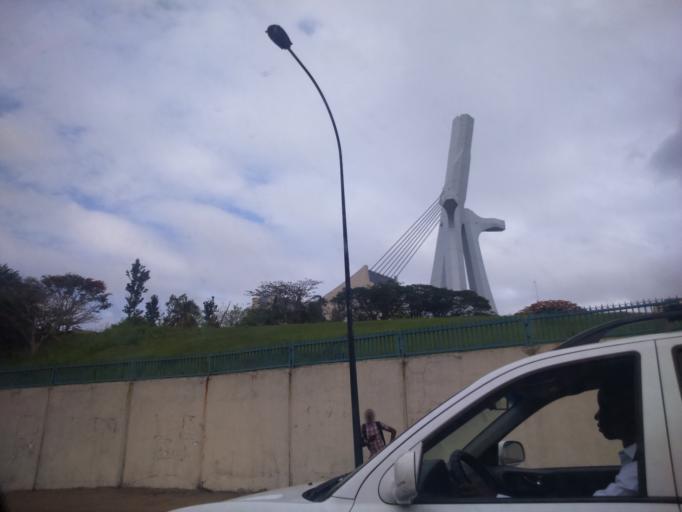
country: CI
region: Lagunes
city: Abidjan
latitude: 5.3339
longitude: -4.0187
